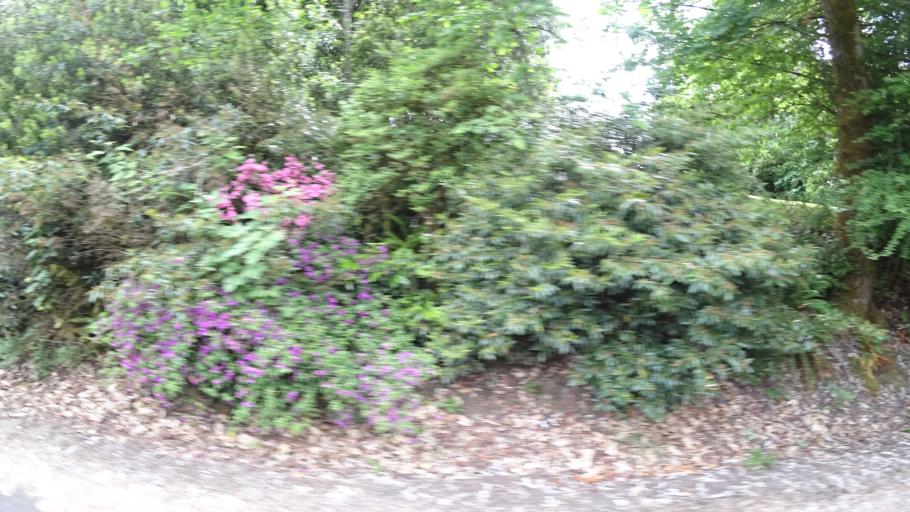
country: US
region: Oregon
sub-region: Clackamas County
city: Lake Oswego
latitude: 45.4510
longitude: -122.6991
